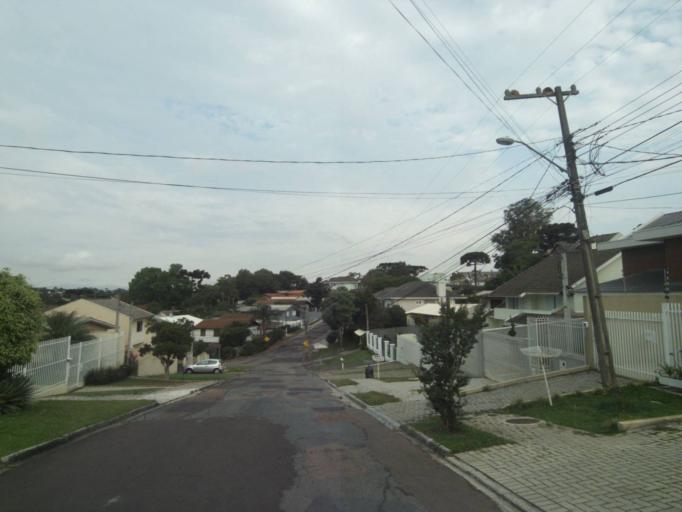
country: BR
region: Parana
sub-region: Curitiba
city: Curitiba
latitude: -25.4008
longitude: -49.2800
